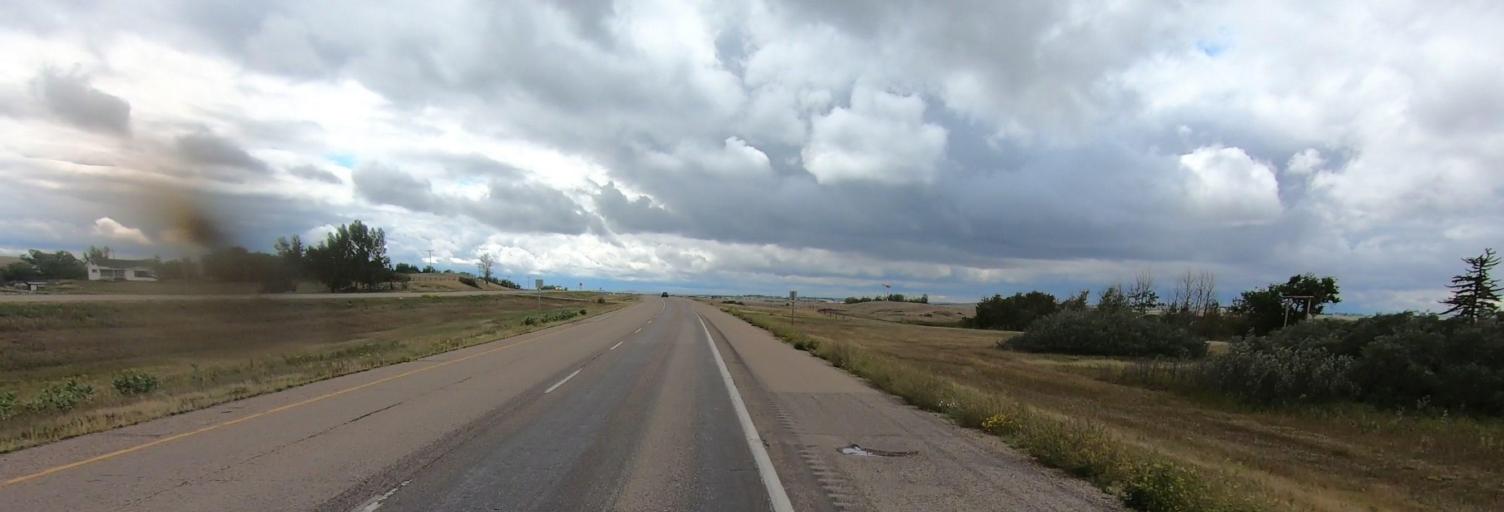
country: CA
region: Saskatchewan
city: Swift Current
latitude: 50.3376
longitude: -107.6867
